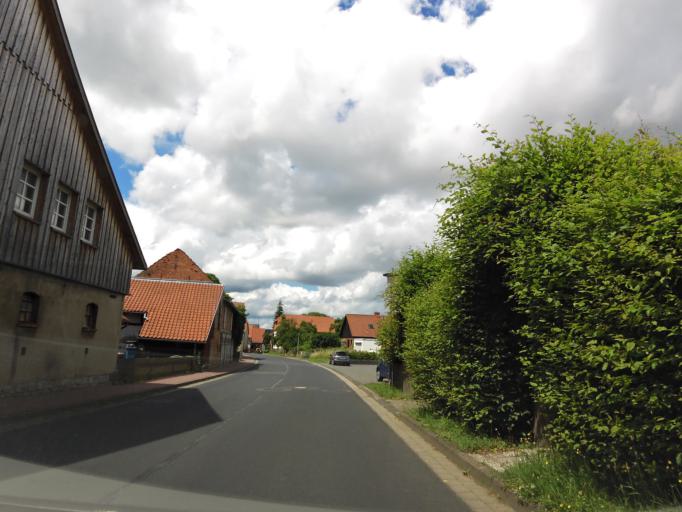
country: DE
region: Lower Saxony
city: Gemeinde Friedland
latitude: 51.4379
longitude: 9.9348
